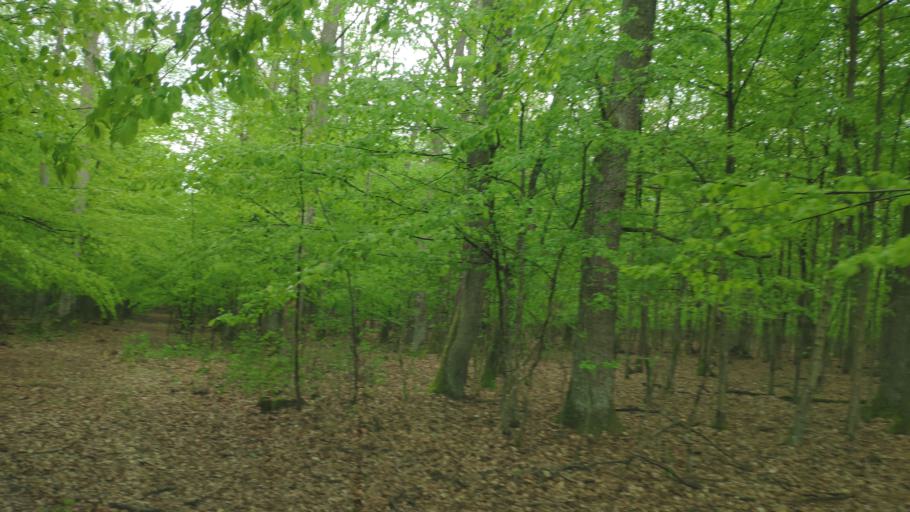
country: SK
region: Kosicky
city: Moldava nad Bodvou
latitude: 48.5469
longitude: 20.9307
